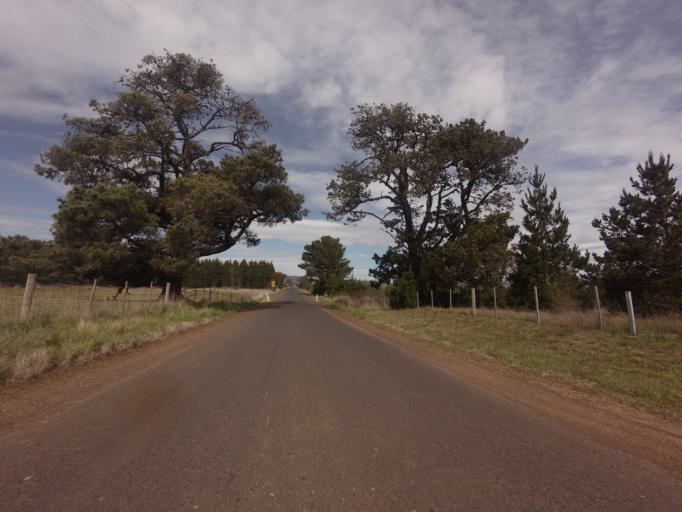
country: AU
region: Tasmania
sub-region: Northern Midlands
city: Evandale
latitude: -41.8619
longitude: 147.3468
